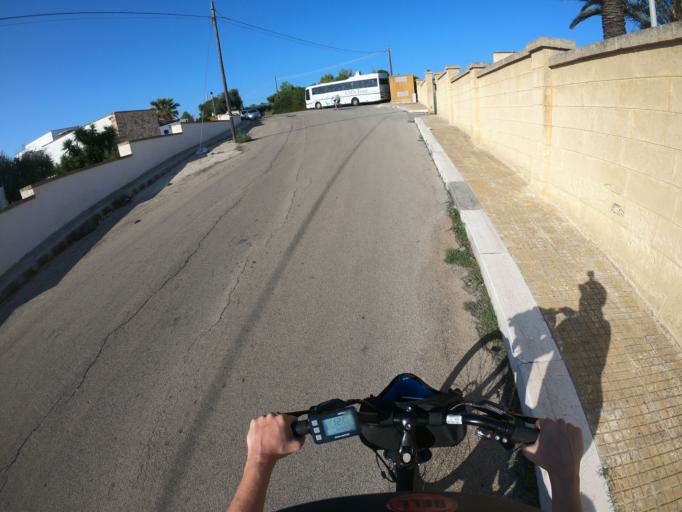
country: IT
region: Apulia
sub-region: Provincia di Lecce
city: Leuca
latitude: 39.8043
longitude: 18.3639
